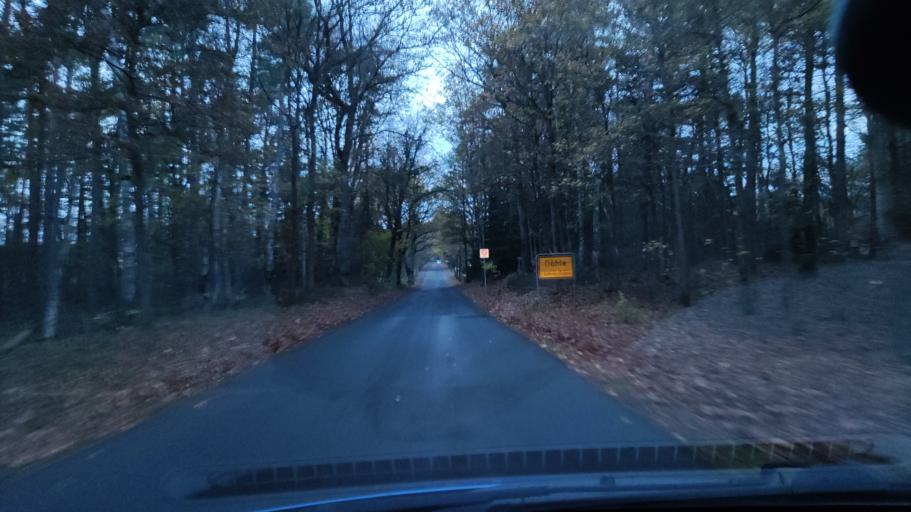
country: DE
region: Lower Saxony
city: Egestorf
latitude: 53.1594
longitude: 10.0349
